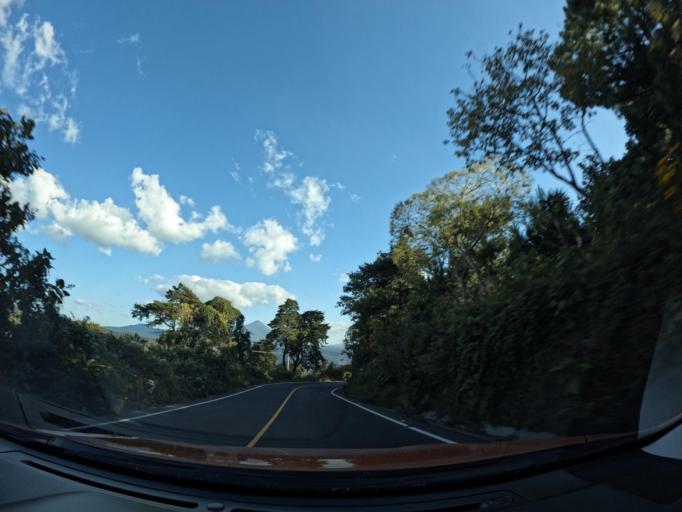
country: GT
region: Escuintla
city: Palin
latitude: 14.4492
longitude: -90.6926
